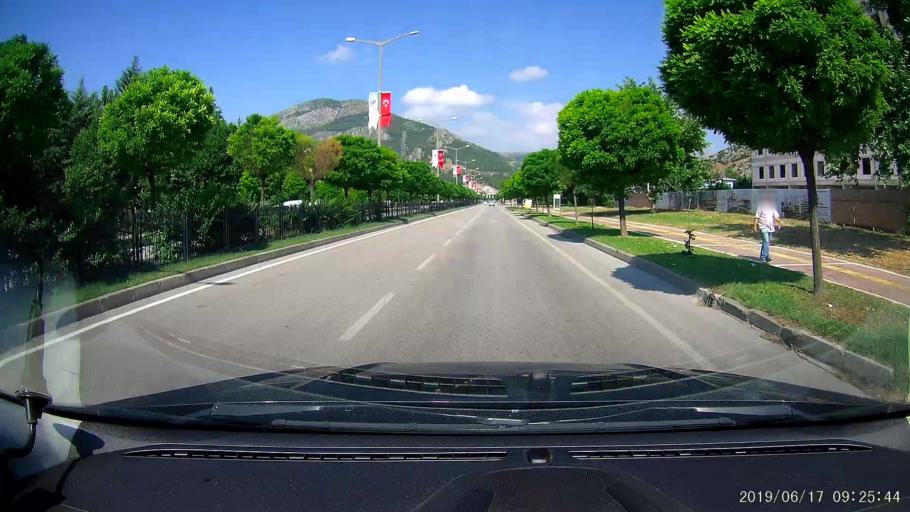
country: TR
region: Amasya
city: Amasya
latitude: 40.6681
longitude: 35.8449
